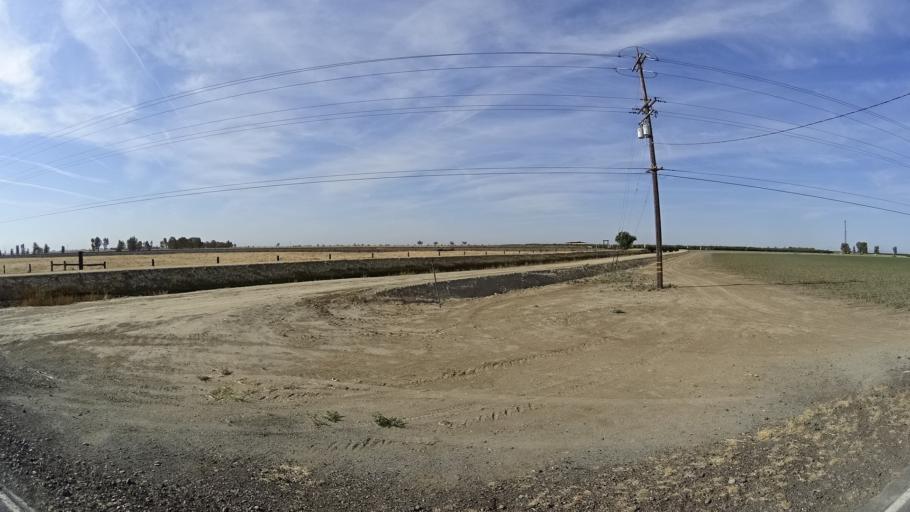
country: US
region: California
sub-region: Kings County
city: Home Garden
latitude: 36.3429
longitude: -119.5411
